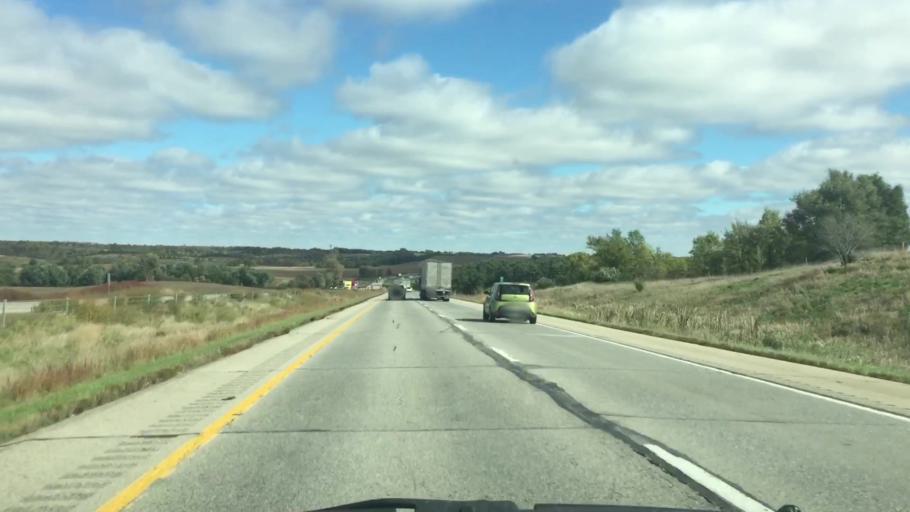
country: US
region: Iowa
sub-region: Poweshiek County
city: Grinnell
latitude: 41.6897
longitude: -92.8743
